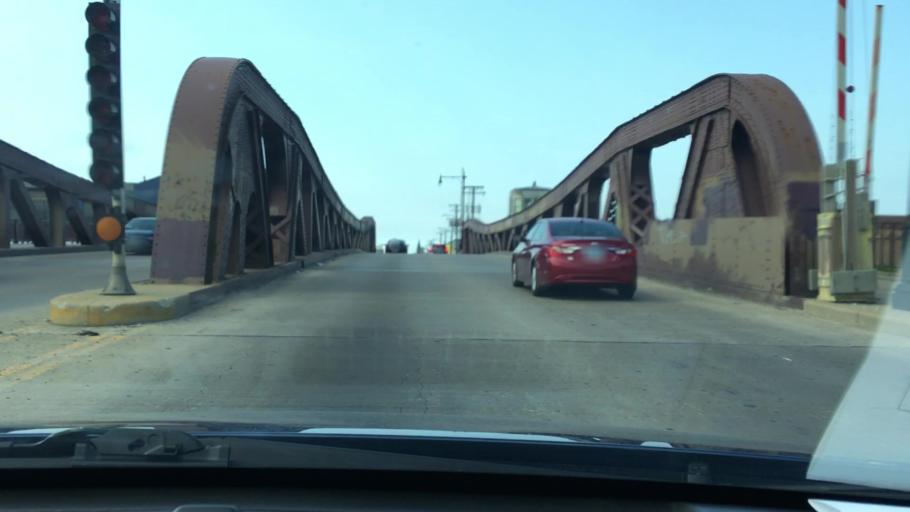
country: US
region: Illinois
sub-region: Cook County
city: Chicago
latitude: 41.8445
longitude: -87.6658
